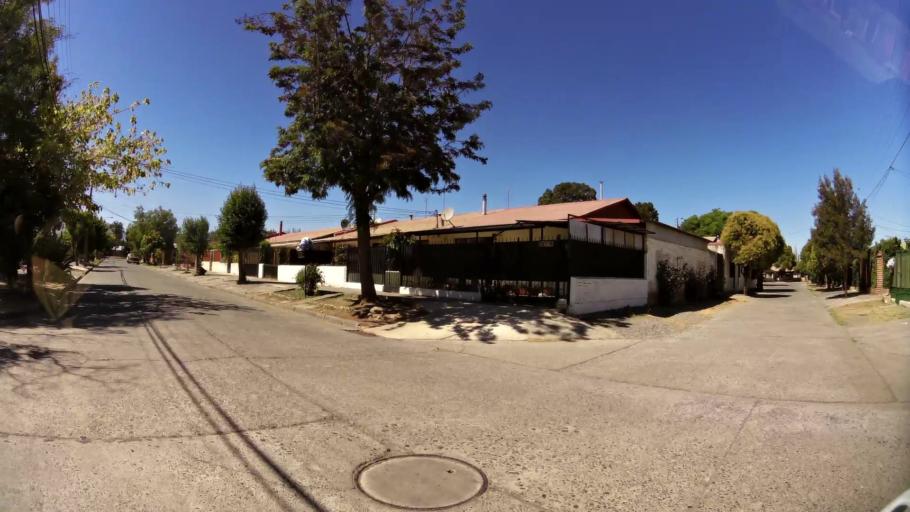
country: CL
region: O'Higgins
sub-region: Provincia de Cachapoal
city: Rancagua
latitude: -34.1759
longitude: -70.7158
